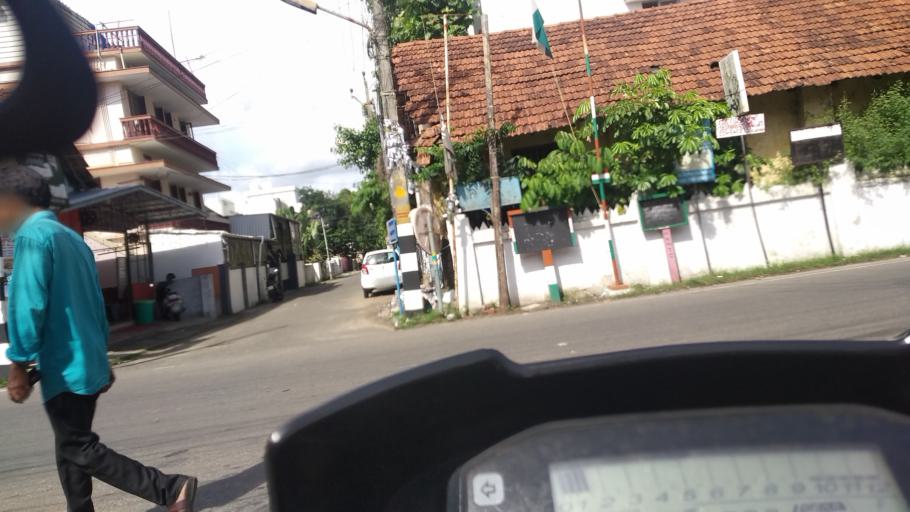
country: IN
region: Kerala
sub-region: Ernakulam
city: Elur
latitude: 10.0228
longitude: 76.2740
